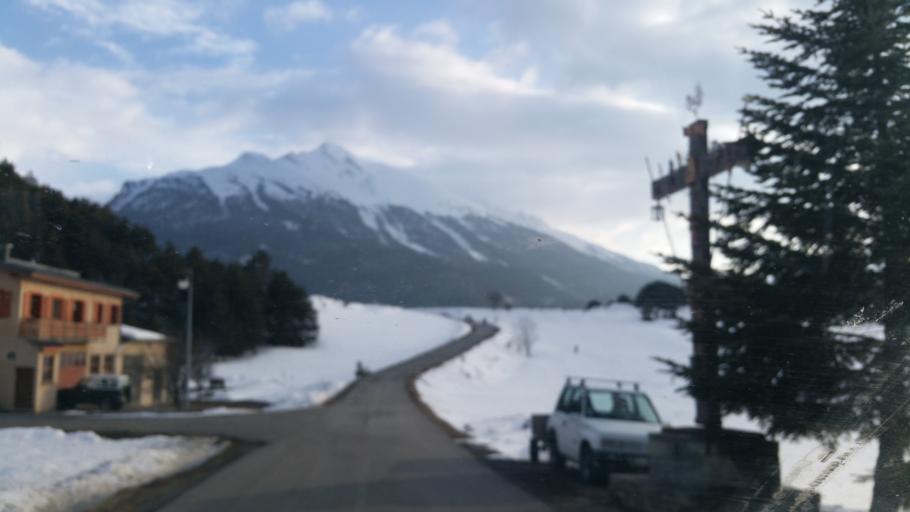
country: FR
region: Rhone-Alpes
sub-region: Departement de la Savoie
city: Modane
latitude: 45.2246
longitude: 6.7410
